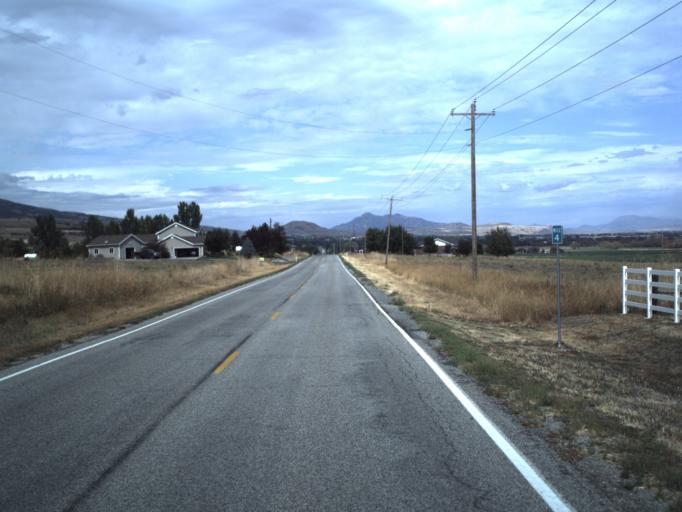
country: US
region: Utah
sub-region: Cache County
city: Wellsville
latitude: 41.6681
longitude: -111.9518
